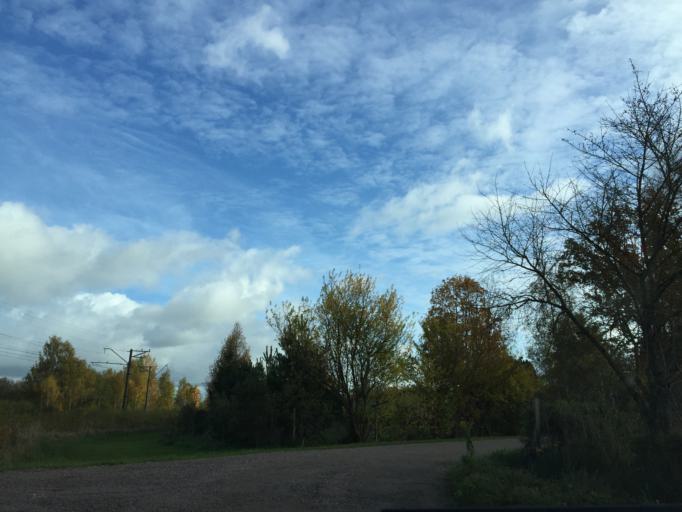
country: LV
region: Lielvarde
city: Lielvarde
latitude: 56.7191
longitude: 24.8304
